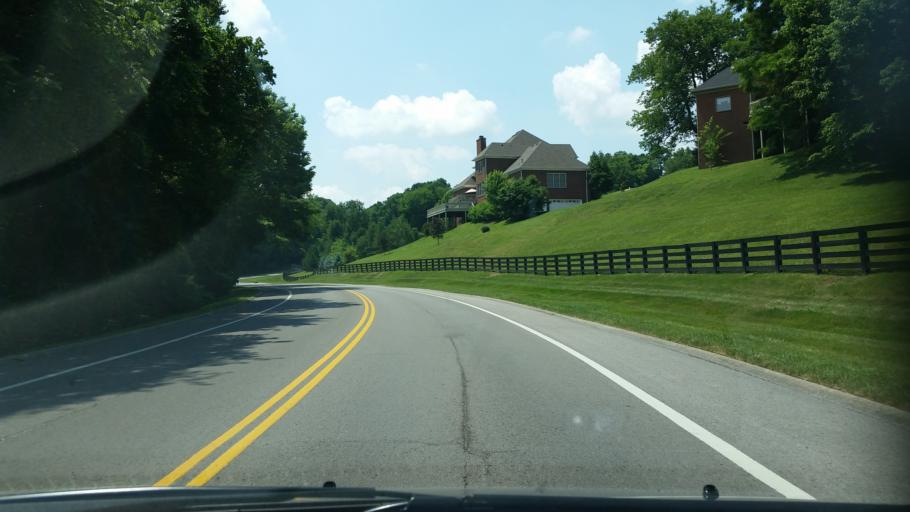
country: US
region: Tennessee
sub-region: Williamson County
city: Brentwood Estates
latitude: 35.9873
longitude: -86.7524
